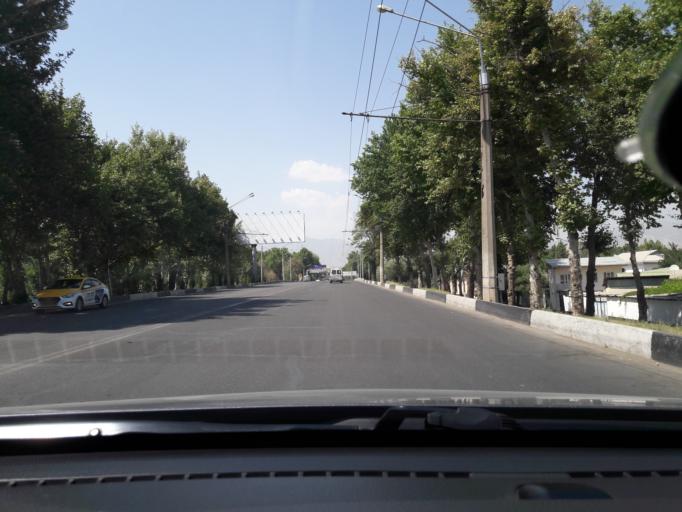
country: TJ
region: Dushanbe
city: Dushanbe
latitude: 38.5747
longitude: 68.7549
